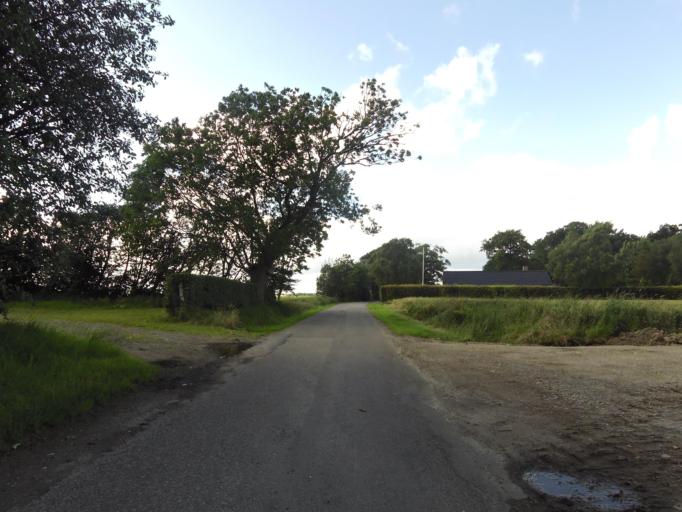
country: DK
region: South Denmark
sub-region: Tonder Kommune
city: Toftlund
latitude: 55.1498
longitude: 9.0857
